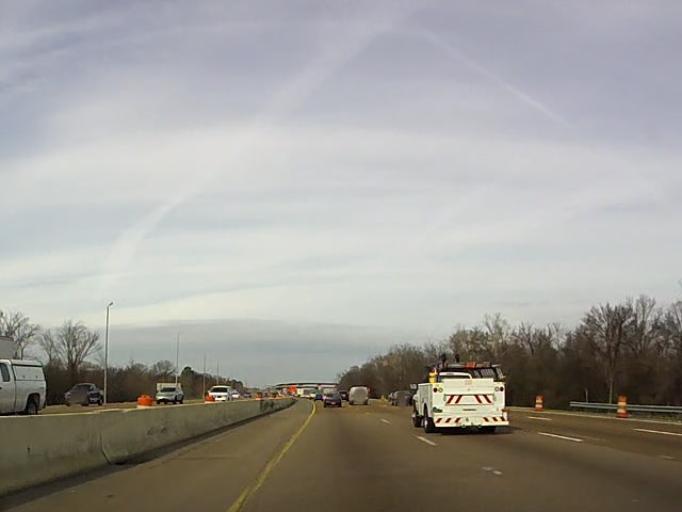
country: US
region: Tennessee
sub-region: Shelby County
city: Bartlett
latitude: 35.1450
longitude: -89.8751
